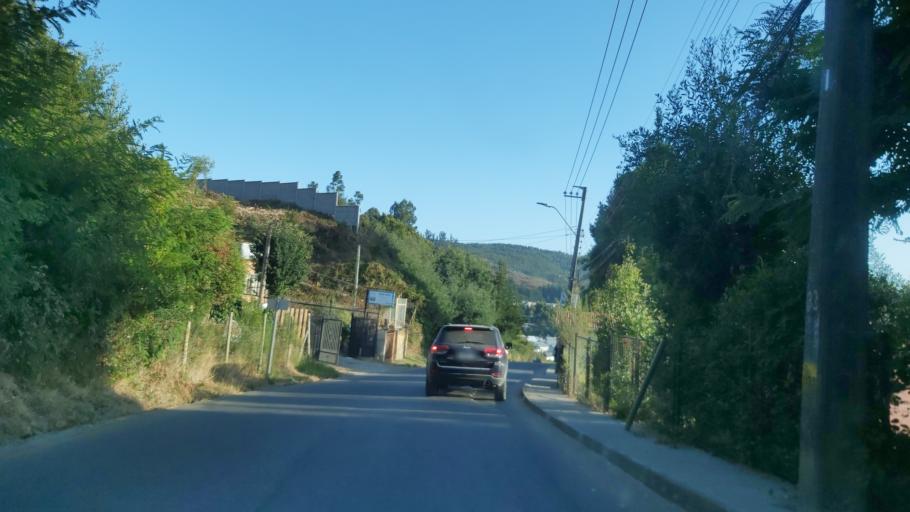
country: CL
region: Biobio
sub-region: Provincia de Concepcion
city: Tome
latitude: -36.5414
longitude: -72.9312
